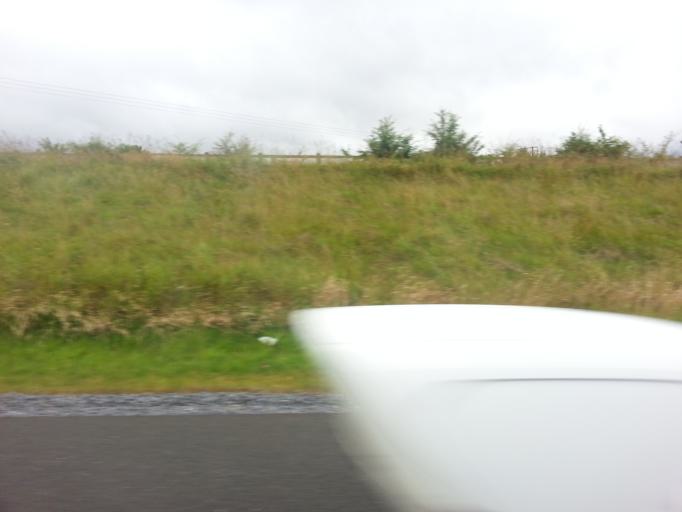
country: IE
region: Leinster
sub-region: Kilkenny
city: Kilkenny
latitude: 52.6566
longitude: -7.2034
